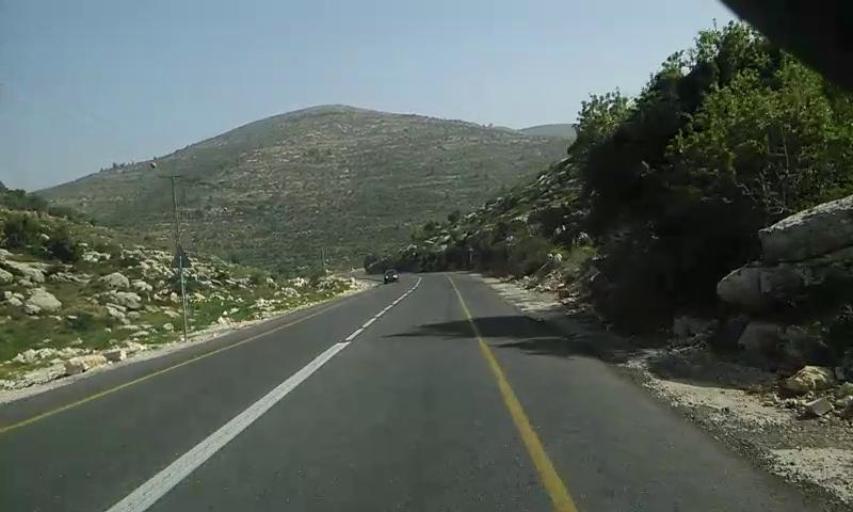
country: PS
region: West Bank
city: `Atarah
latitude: 32.0006
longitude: 35.2267
